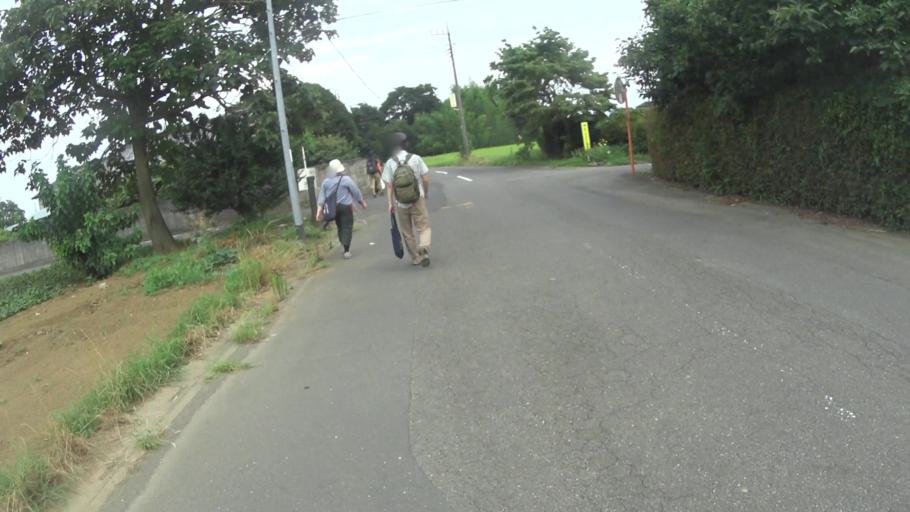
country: JP
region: Saitama
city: Okegawa
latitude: 35.9624
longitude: 139.5438
